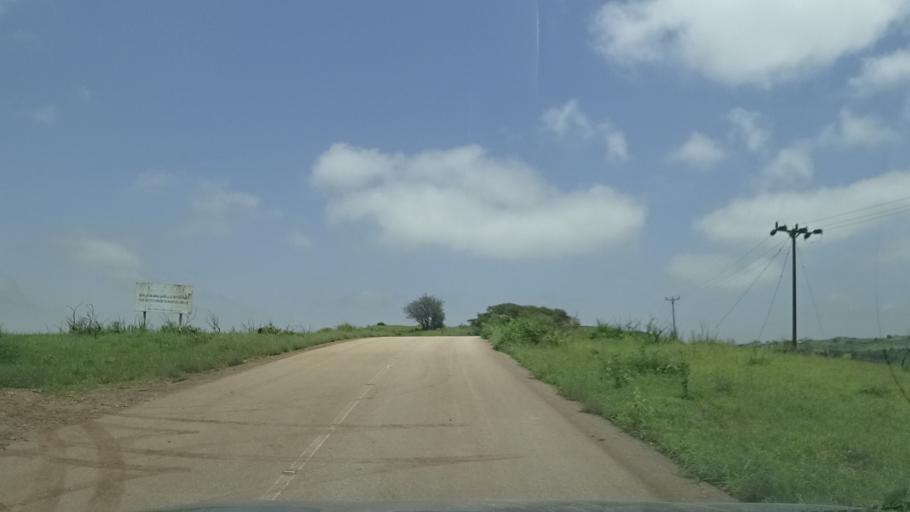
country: OM
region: Zufar
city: Salalah
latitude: 17.2161
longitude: 54.2003
